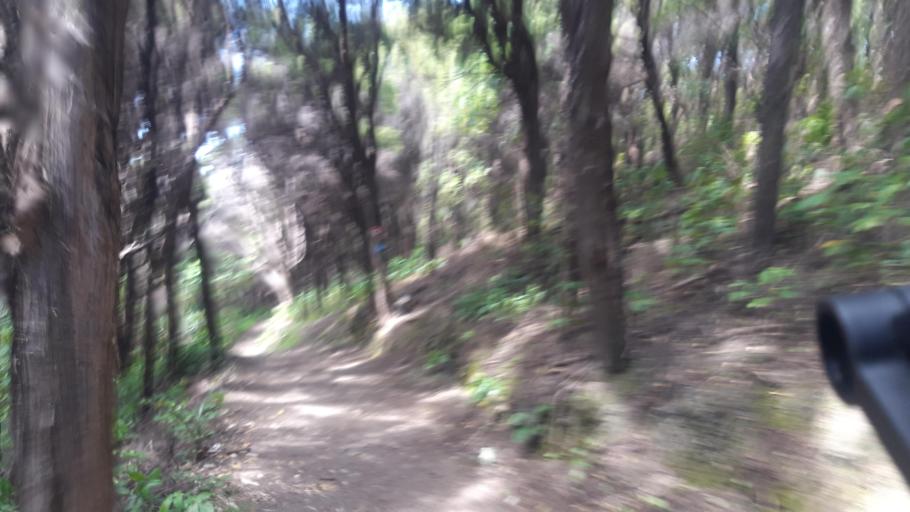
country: NZ
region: Marlborough
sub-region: Marlborough District
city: Picton
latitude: -41.2547
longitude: 174.0417
